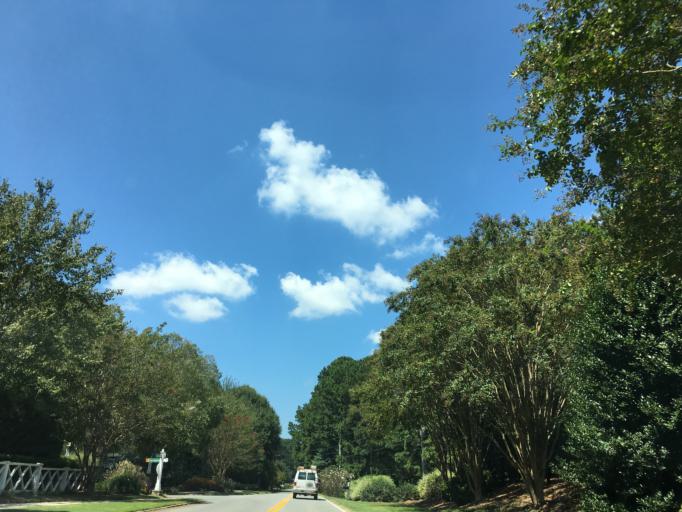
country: US
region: Georgia
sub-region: Fulton County
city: Milton
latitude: 34.1167
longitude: -84.3012
